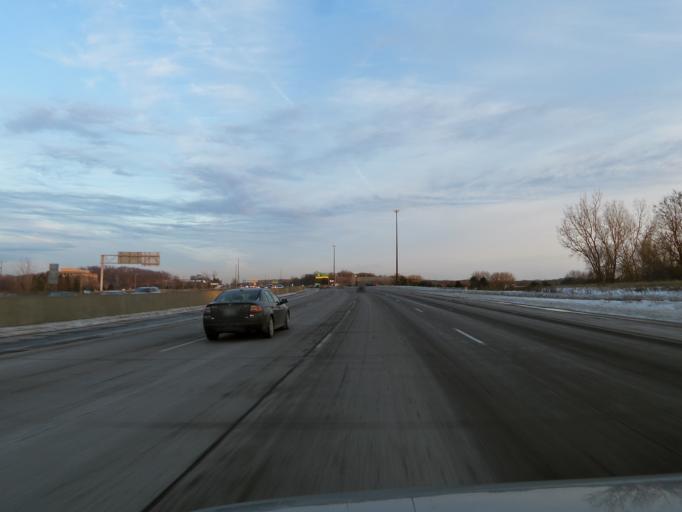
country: US
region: Minnesota
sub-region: Hennepin County
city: Eden Prairie
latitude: 44.8594
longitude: -93.4170
